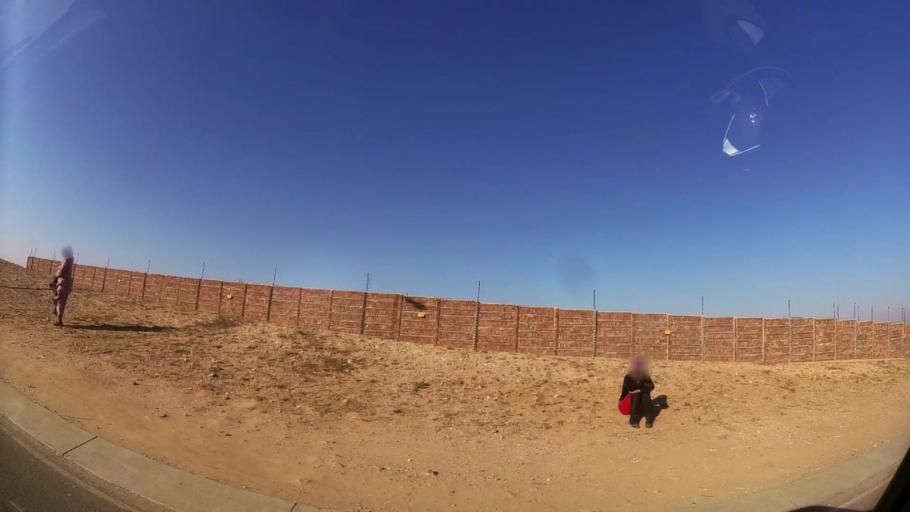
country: ZA
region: Gauteng
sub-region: City of Johannesburg Metropolitan Municipality
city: Midrand
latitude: -25.9072
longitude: 28.1048
